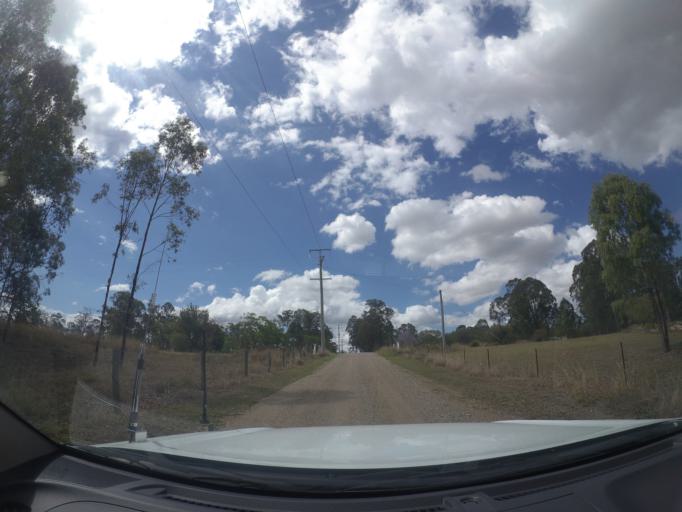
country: AU
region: Queensland
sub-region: Logan
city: Cedar Vale
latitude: -27.8974
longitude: 153.0010
